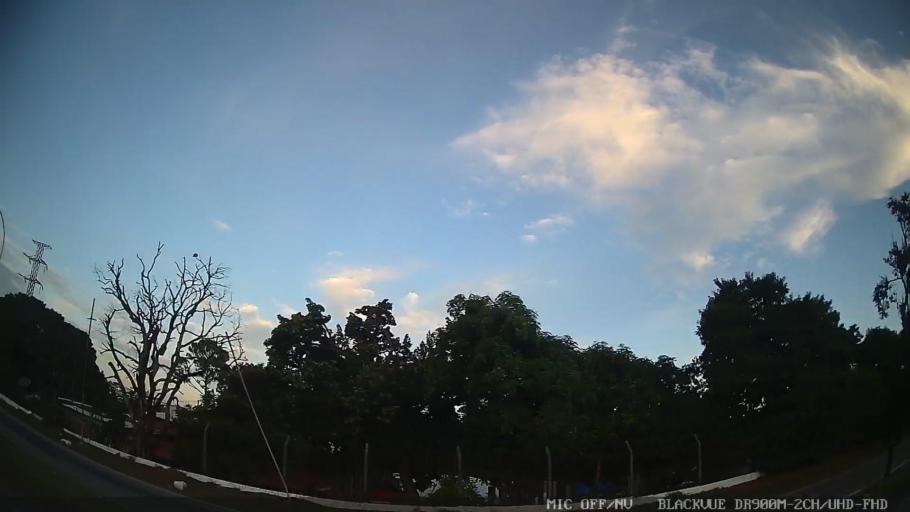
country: BR
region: Sao Paulo
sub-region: Indaiatuba
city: Indaiatuba
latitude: -23.1382
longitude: -47.2430
